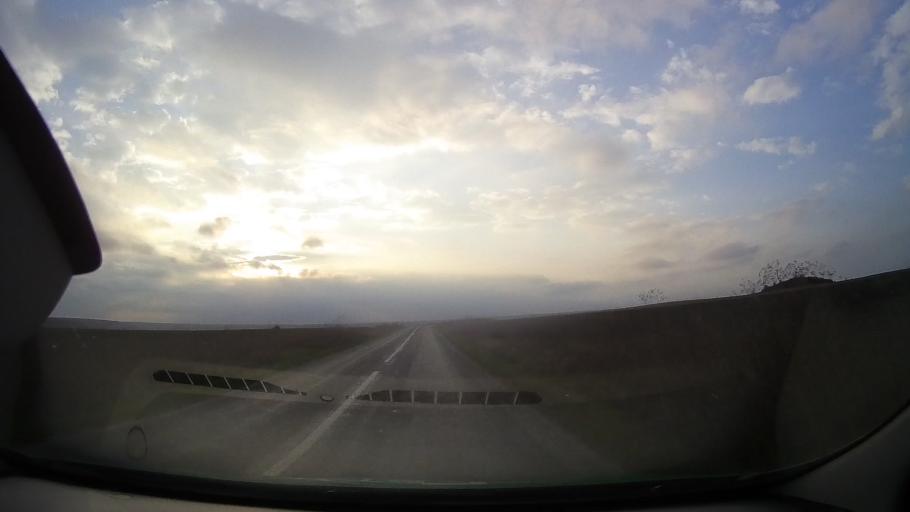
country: RO
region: Constanta
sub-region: Comuna Adamclisi
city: Adamclisi
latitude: 44.0170
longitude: 27.9008
